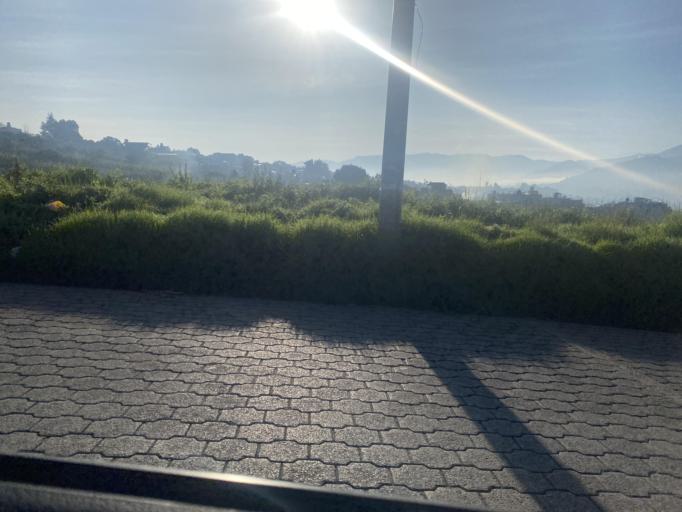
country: GT
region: Quetzaltenango
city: Quetzaltenango
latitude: 14.8535
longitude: -91.5179
